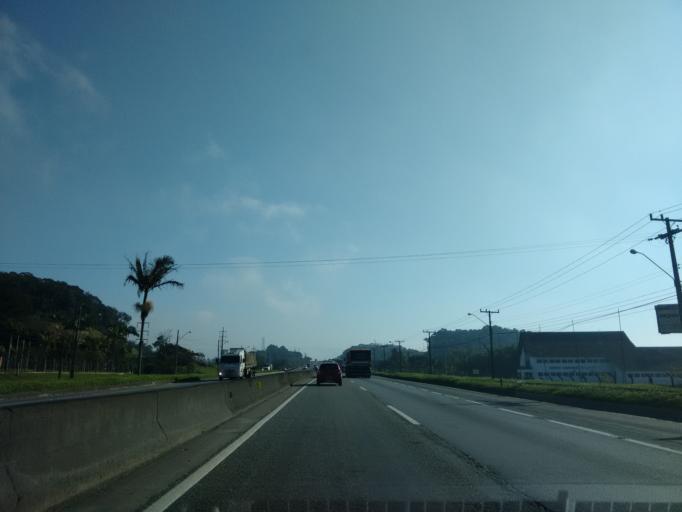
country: BR
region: Santa Catarina
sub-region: Joinville
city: Joinville
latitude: -26.3001
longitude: -48.8835
